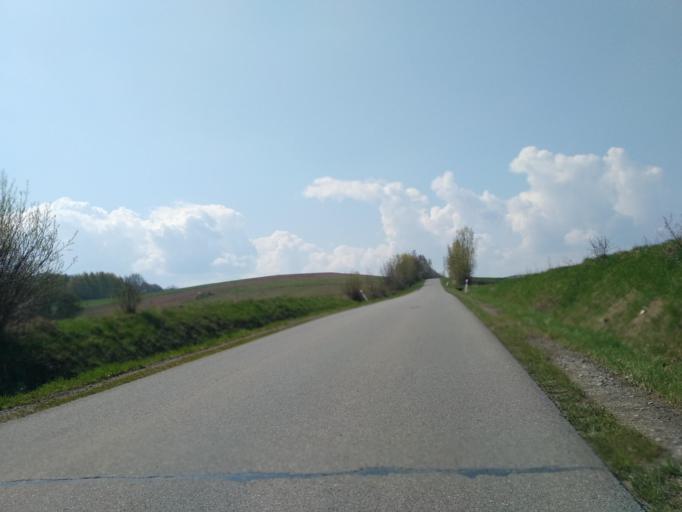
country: PL
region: Subcarpathian Voivodeship
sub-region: Powiat sanocki
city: Zarszyn
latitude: 49.5667
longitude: 22.0019
